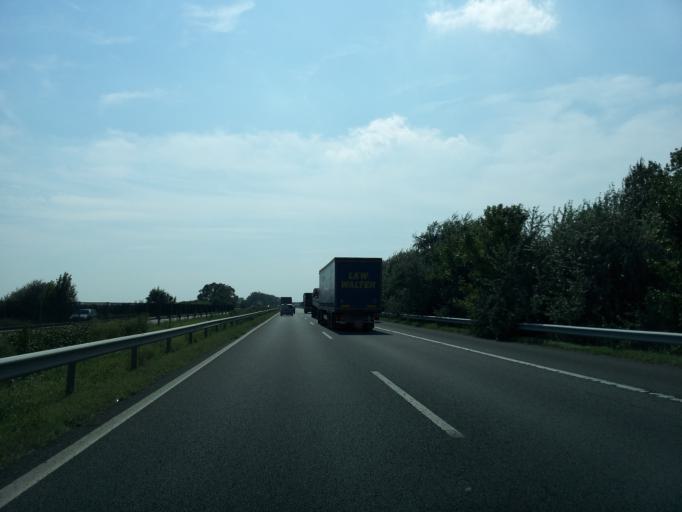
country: HU
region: Fejer
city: Baracska
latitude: 47.2810
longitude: 18.7101
